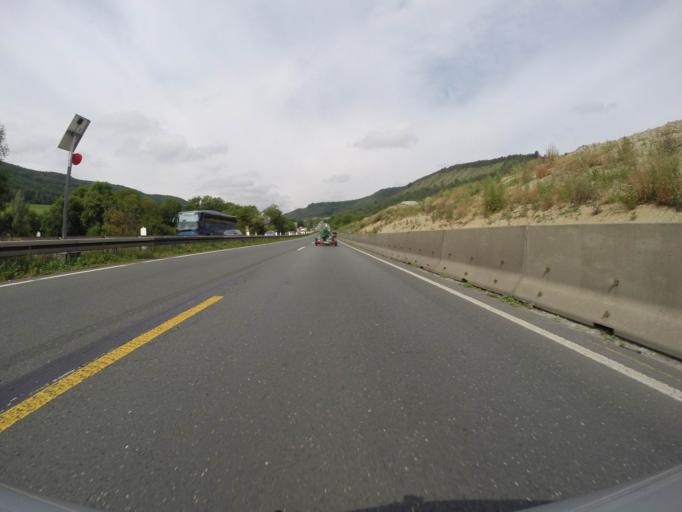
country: DE
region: Thuringia
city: Rothenstein
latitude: 50.8704
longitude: 11.5812
